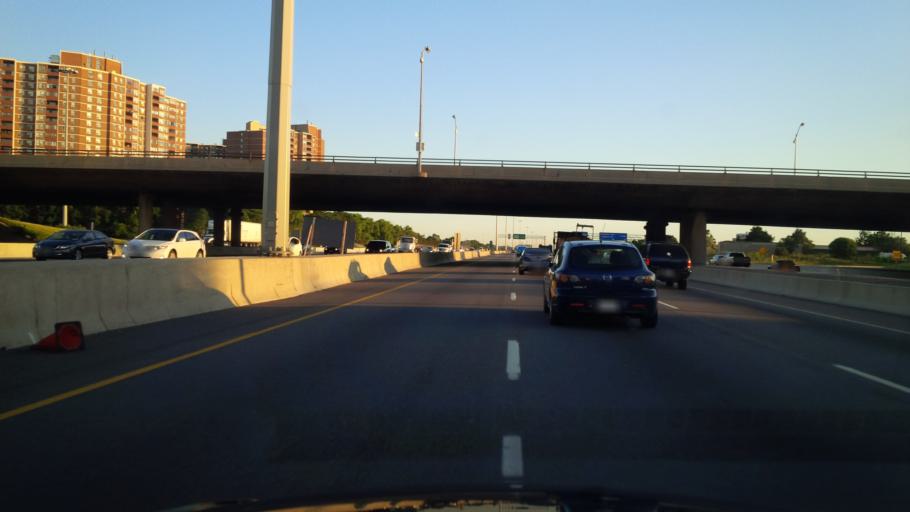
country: CA
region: Ontario
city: Etobicoke
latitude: 43.6537
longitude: -79.5671
